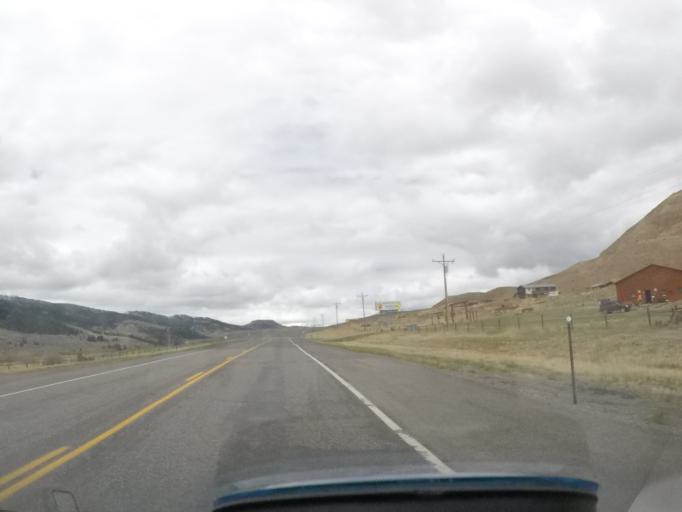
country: US
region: Wyoming
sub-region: Sublette County
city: Pinedale
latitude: 43.5713
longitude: -109.7203
